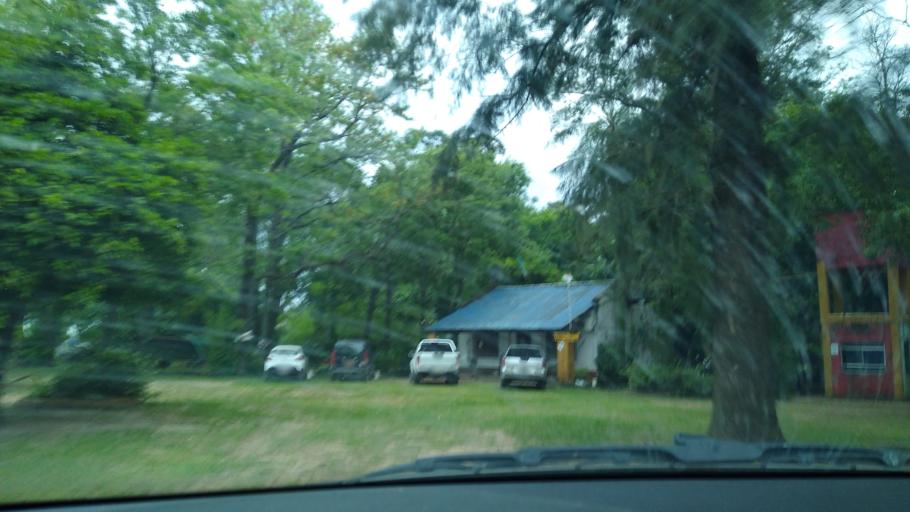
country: AR
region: Chaco
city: Puerto Vilelas
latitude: -27.5141
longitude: -58.9716
